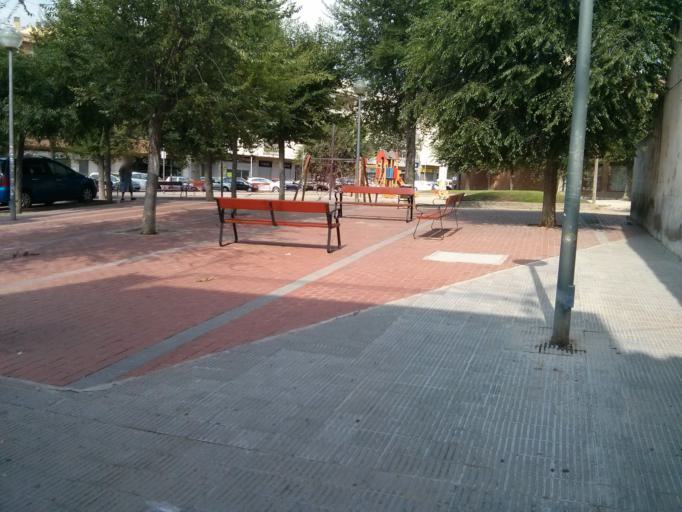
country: ES
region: Catalonia
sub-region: Provincia de Tarragona
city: El Vendrell
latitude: 41.2166
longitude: 1.5315
